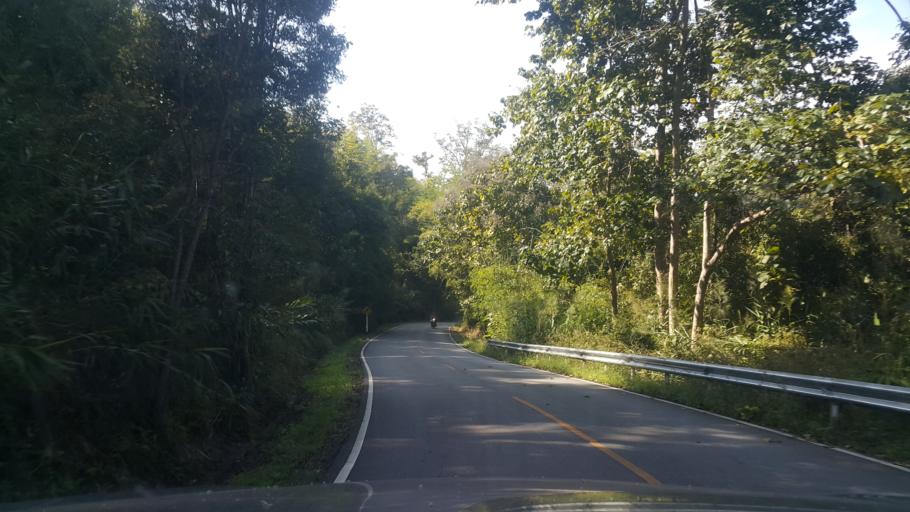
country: TH
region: Chiang Mai
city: Samoeng
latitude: 18.9087
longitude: 98.6758
